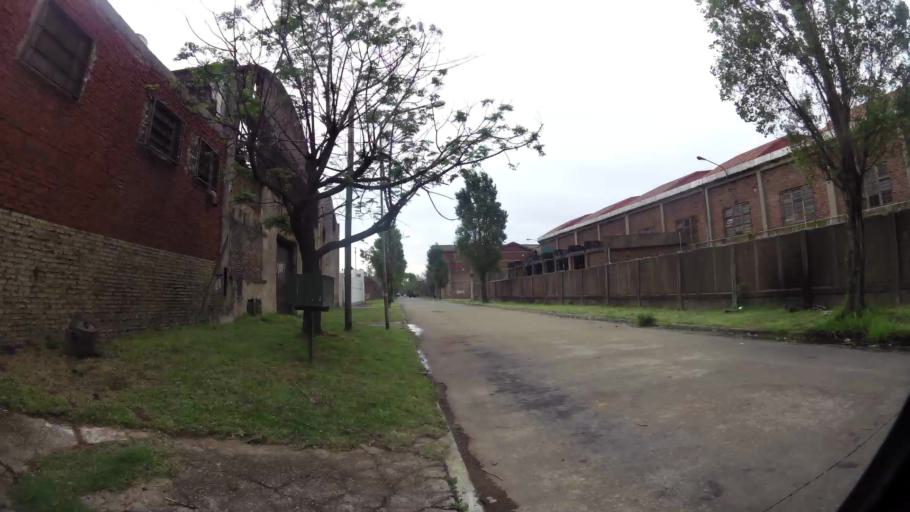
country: AR
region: Buenos Aires
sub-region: Partido de Lanus
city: Lanus
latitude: -34.7131
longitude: -58.3583
